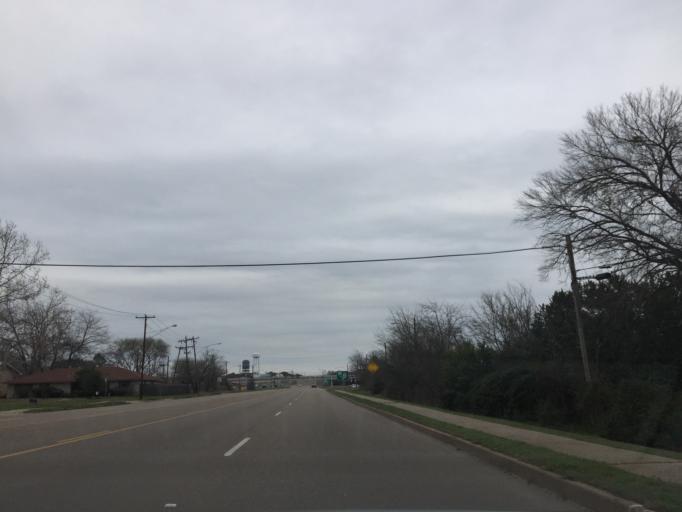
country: US
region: Texas
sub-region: Coryell County
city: Gatesville
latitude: 31.4346
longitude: -97.7194
